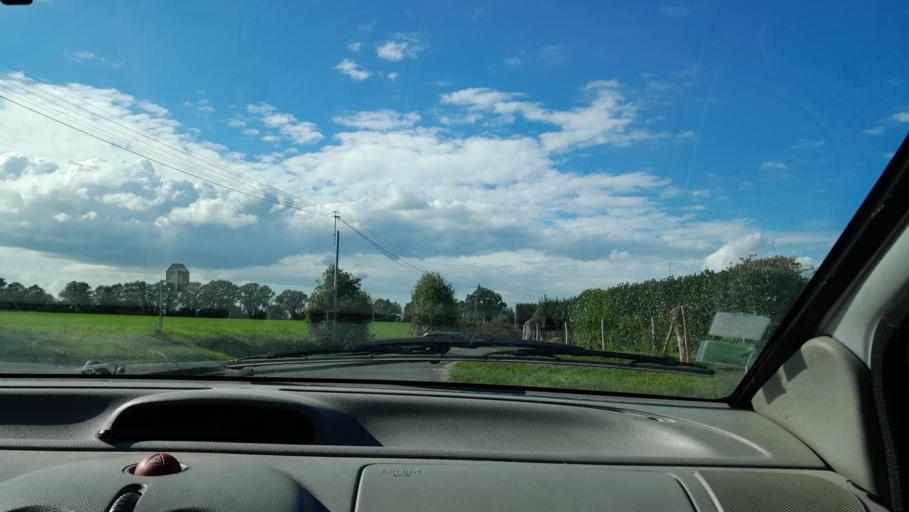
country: FR
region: Pays de la Loire
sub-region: Departement de la Mayenne
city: Ahuille
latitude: 48.0357
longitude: -0.8968
